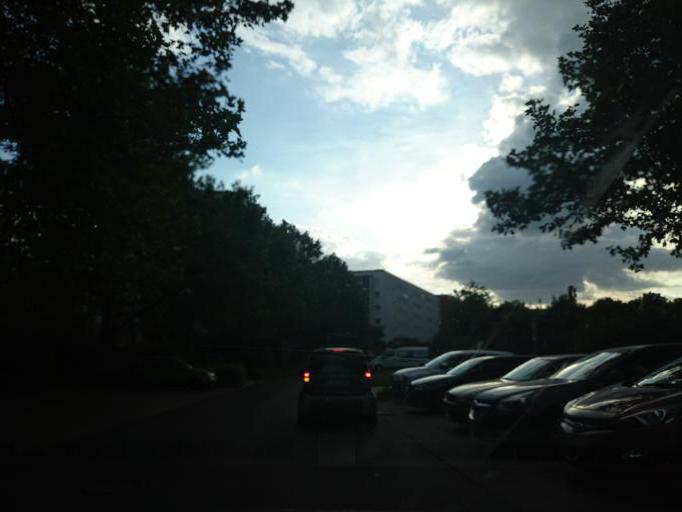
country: DE
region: Berlin
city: Hellersdorf
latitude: 52.5364
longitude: 13.5960
